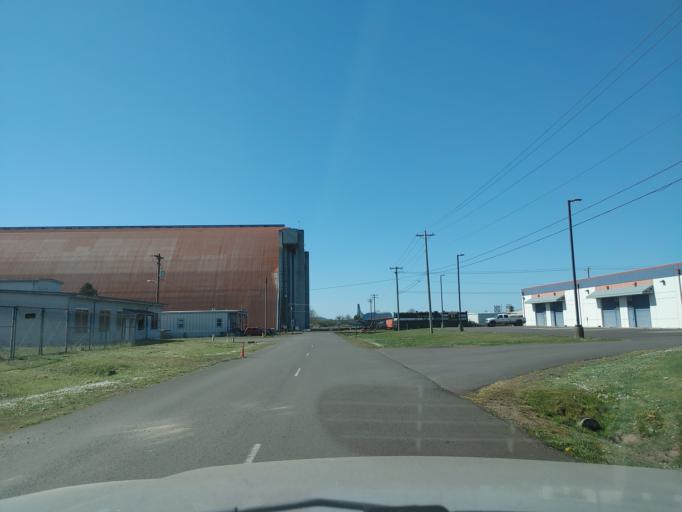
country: US
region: Oregon
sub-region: Tillamook County
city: Tillamook
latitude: 45.4201
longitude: -123.8008
